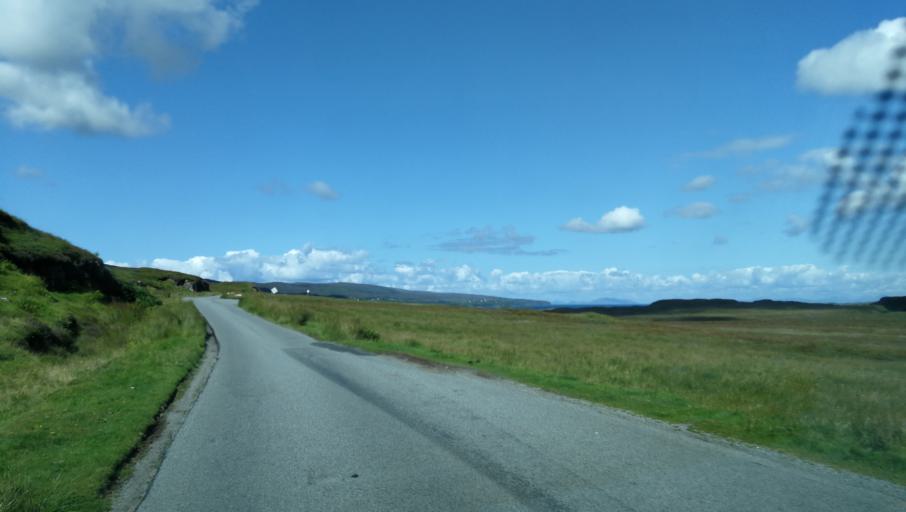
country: GB
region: Scotland
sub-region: Highland
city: Isle of Skye
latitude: 57.4266
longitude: -6.6025
